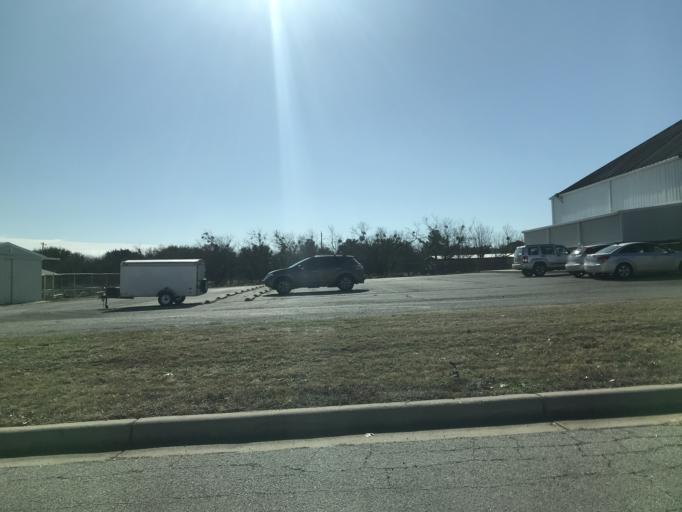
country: US
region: Texas
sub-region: Taylor County
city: Abilene
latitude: 32.3819
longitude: -99.7691
